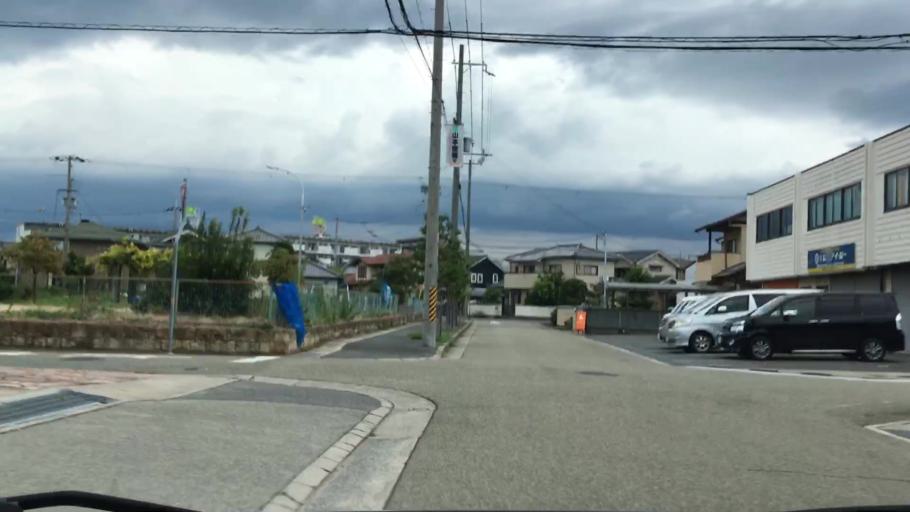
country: JP
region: Hyogo
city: Himeji
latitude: 34.8151
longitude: 134.6943
